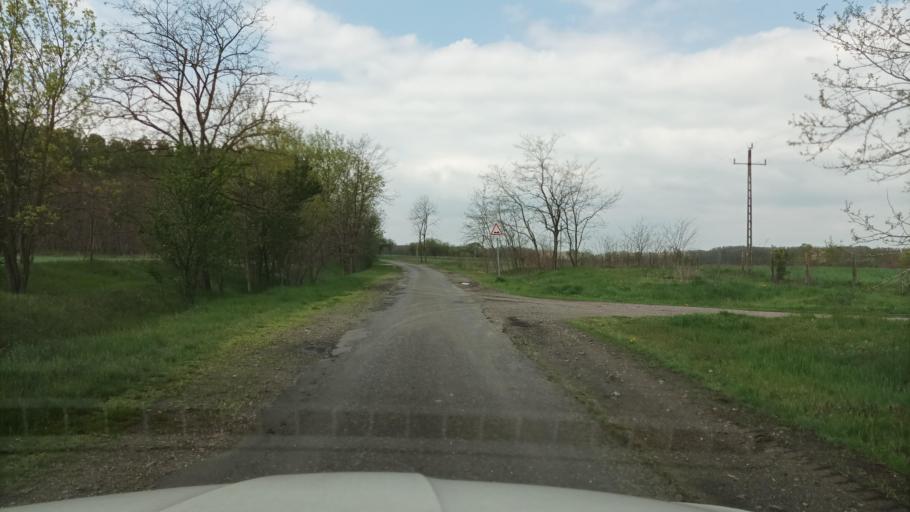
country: HU
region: Pest
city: Kocser
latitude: 47.0525
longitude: 19.8797
